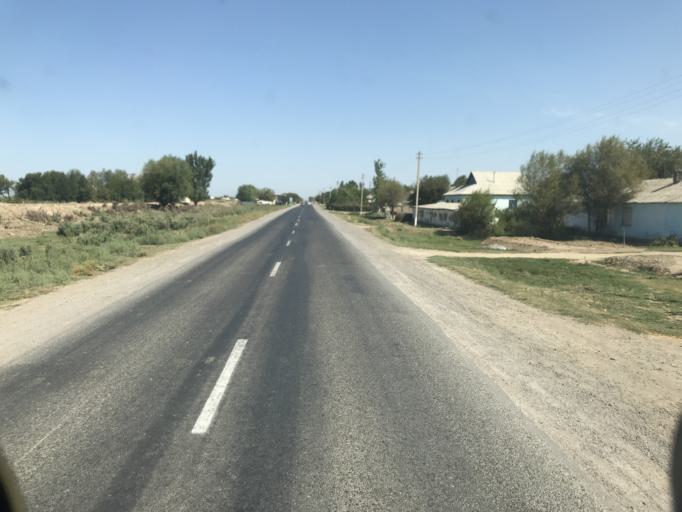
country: KZ
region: Ongtustik Qazaqstan
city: Myrzakent
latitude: 40.7574
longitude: 68.5370
